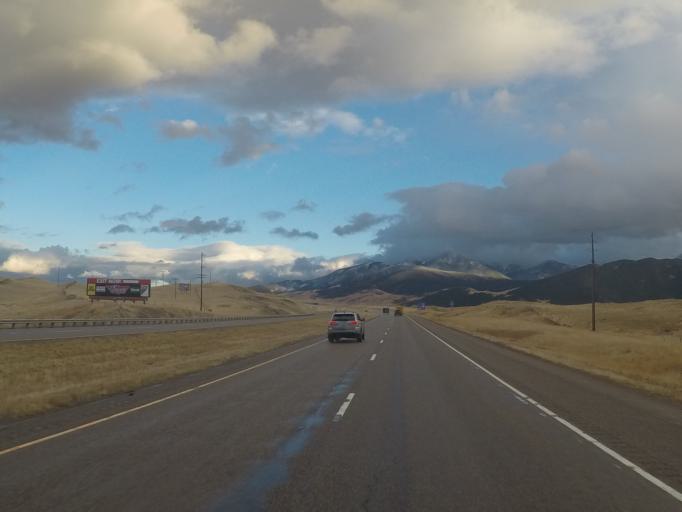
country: US
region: Montana
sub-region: Park County
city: Livingston
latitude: 45.6491
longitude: -110.6058
